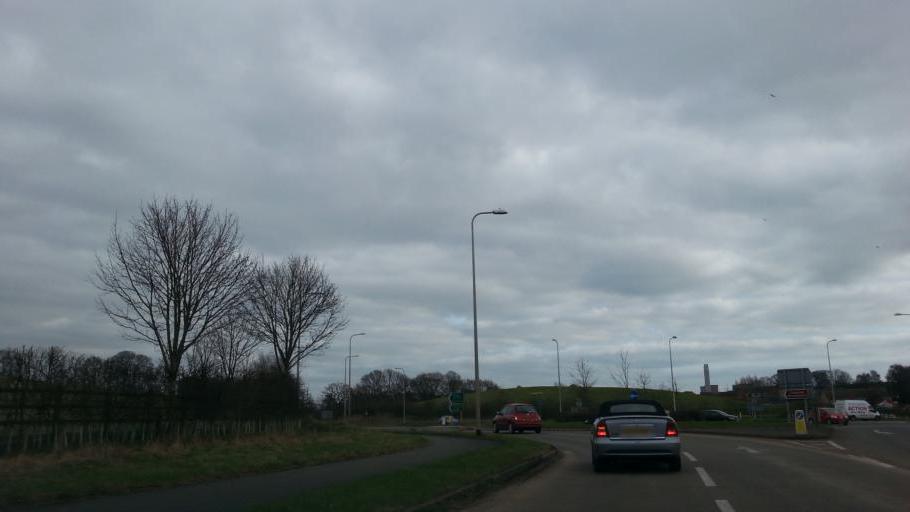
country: GB
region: England
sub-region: Staffordshire
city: Rugeley
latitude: 52.7757
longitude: -1.9517
